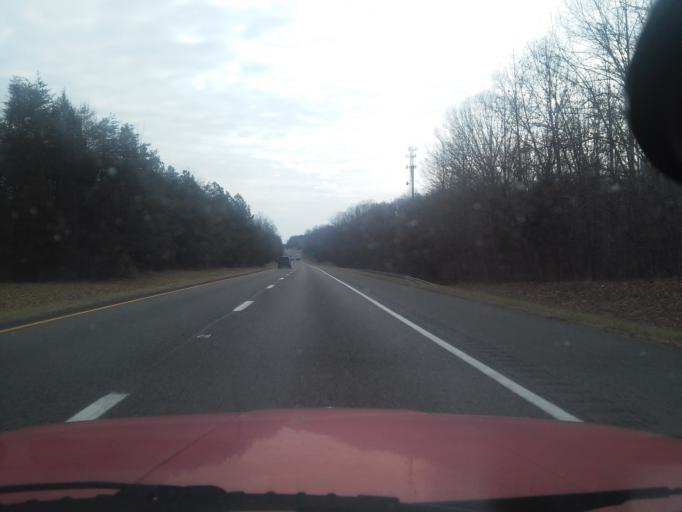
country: US
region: Virginia
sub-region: Louisa County
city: Louisa
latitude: 37.8925
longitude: -78.0410
